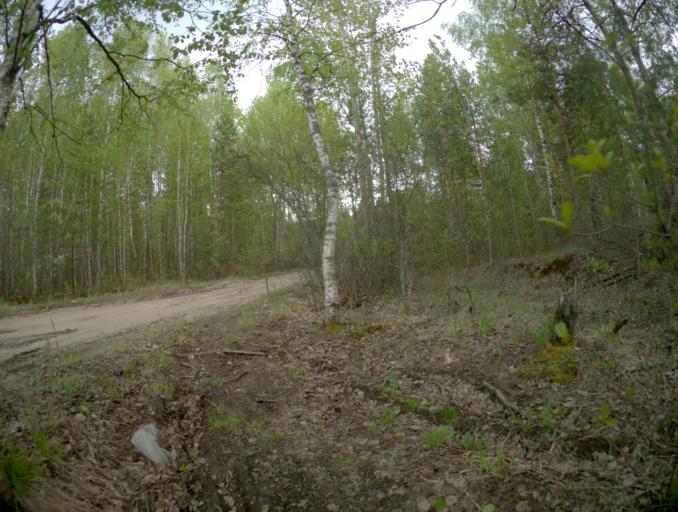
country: RU
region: Moskovskaya
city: Cherusti
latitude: 55.5835
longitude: 40.0461
